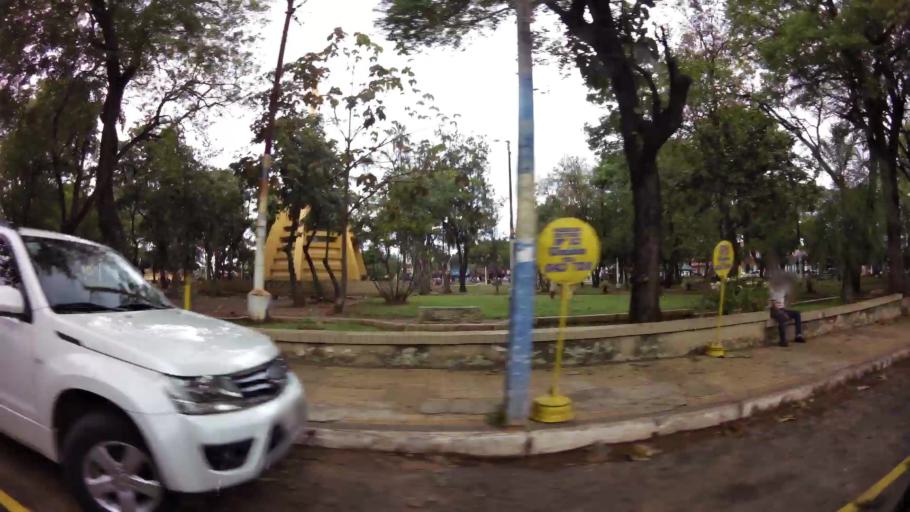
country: PY
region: Central
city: San Lorenzo
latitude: -25.2662
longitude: -57.4946
